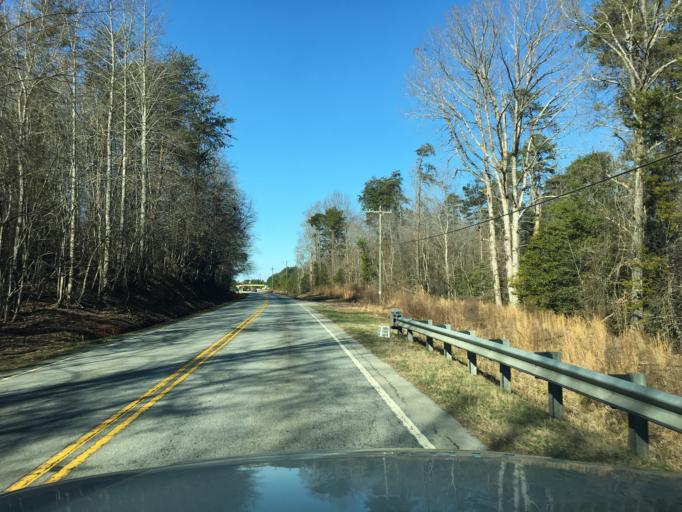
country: US
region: South Carolina
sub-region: Greenville County
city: Berea
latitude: 34.8898
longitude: -82.5292
